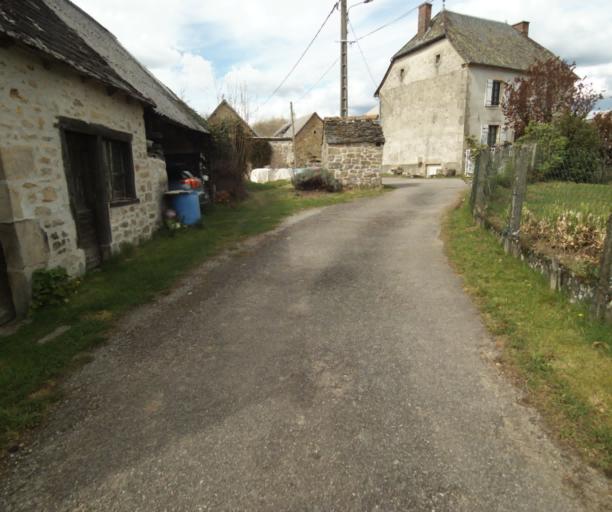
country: FR
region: Limousin
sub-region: Departement de la Correze
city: Argentat
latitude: 45.1818
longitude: 1.9369
